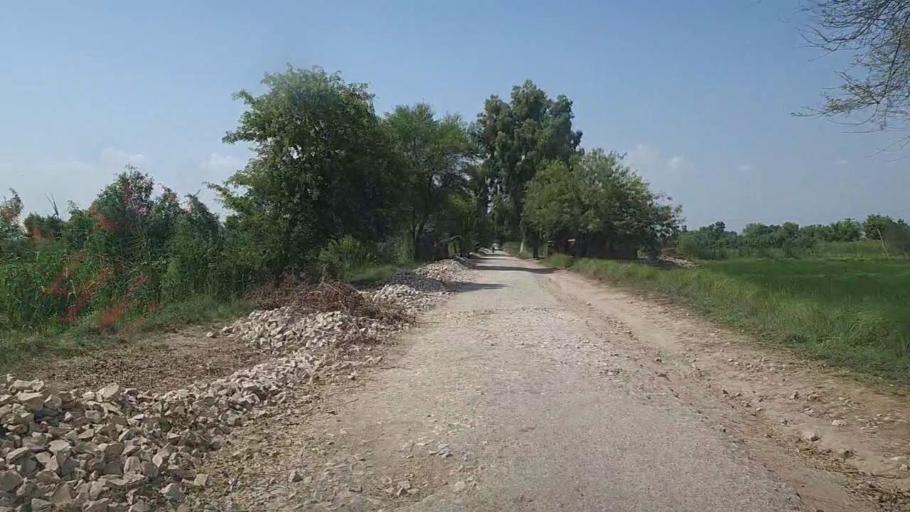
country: PK
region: Sindh
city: Khairpur
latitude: 28.0853
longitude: 69.6339
